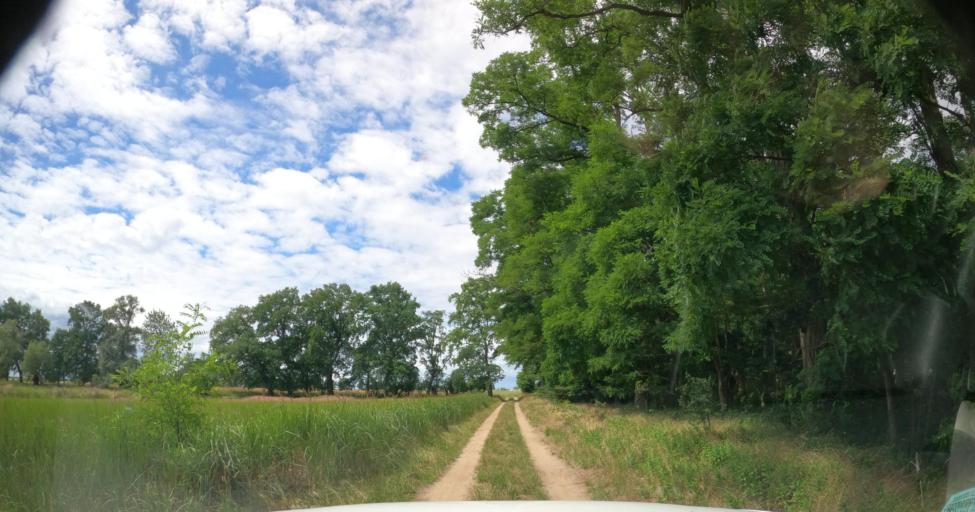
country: PL
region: West Pomeranian Voivodeship
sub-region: Powiat goleniowski
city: Stepnica
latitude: 53.7002
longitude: 14.5475
